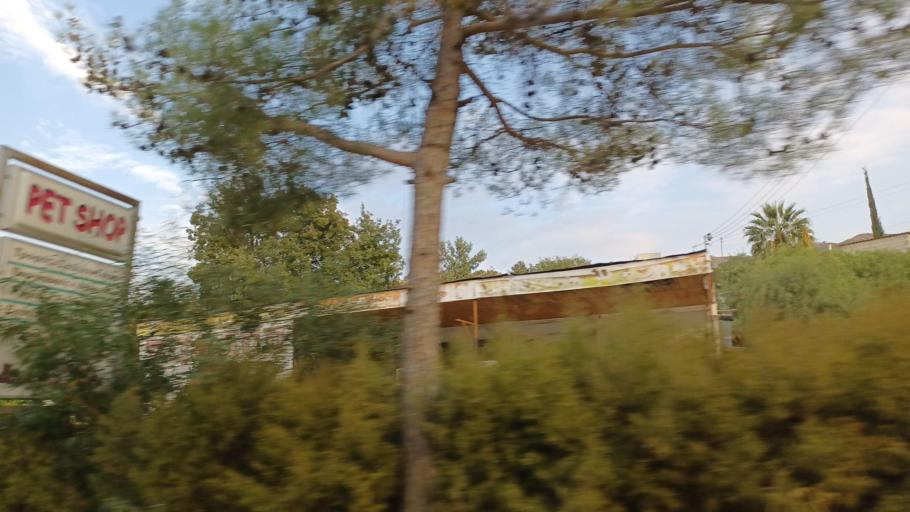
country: CY
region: Lefkosia
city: Kakopetria
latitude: 35.0310
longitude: 32.9007
